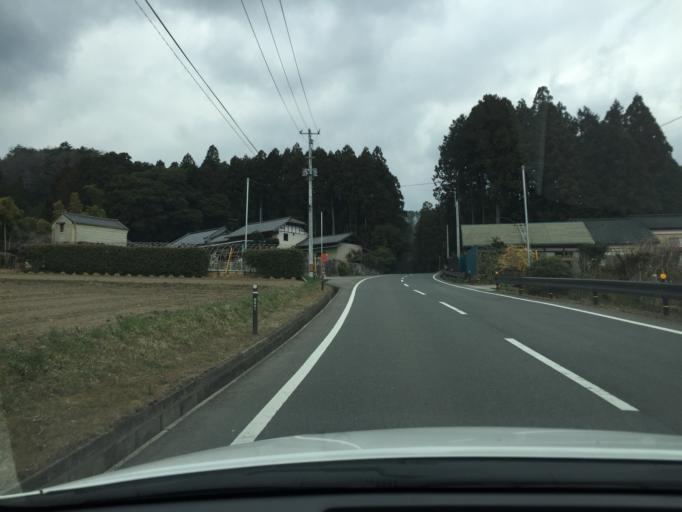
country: JP
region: Miyagi
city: Marumori
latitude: 37.7915
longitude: 140.8851
